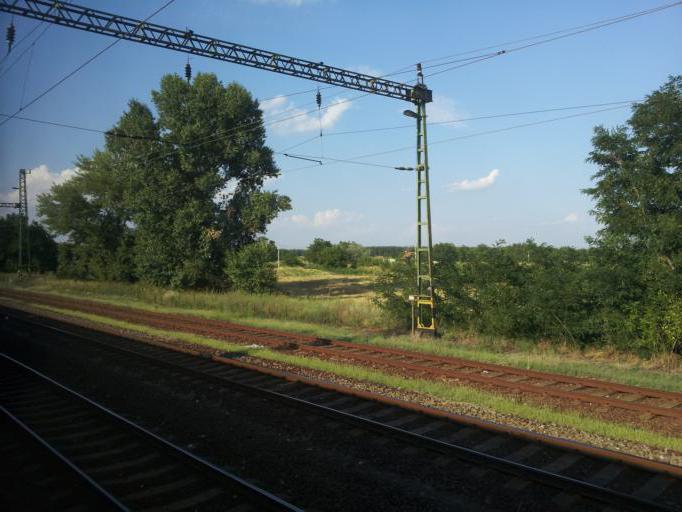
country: HU
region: Pest
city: Taksony
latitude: 47.3233
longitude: 19.0777
